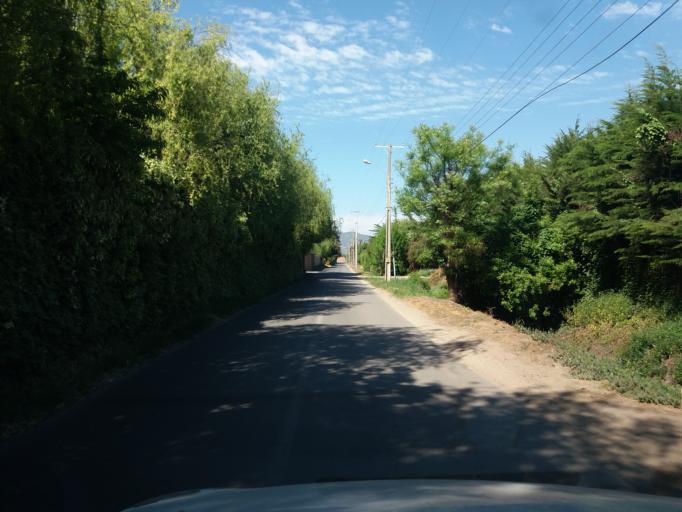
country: CL
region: Valparaiso
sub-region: Provincia de Quillota
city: Quillota
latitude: -32.8727
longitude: -71.2190
